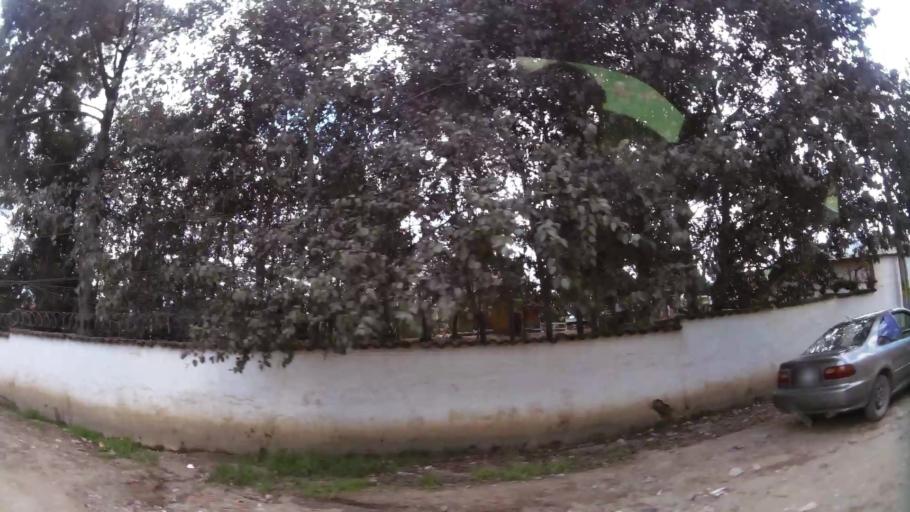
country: GT
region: Quetzaltenango
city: Quetzaltenango
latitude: 14.8404
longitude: -91.5376
